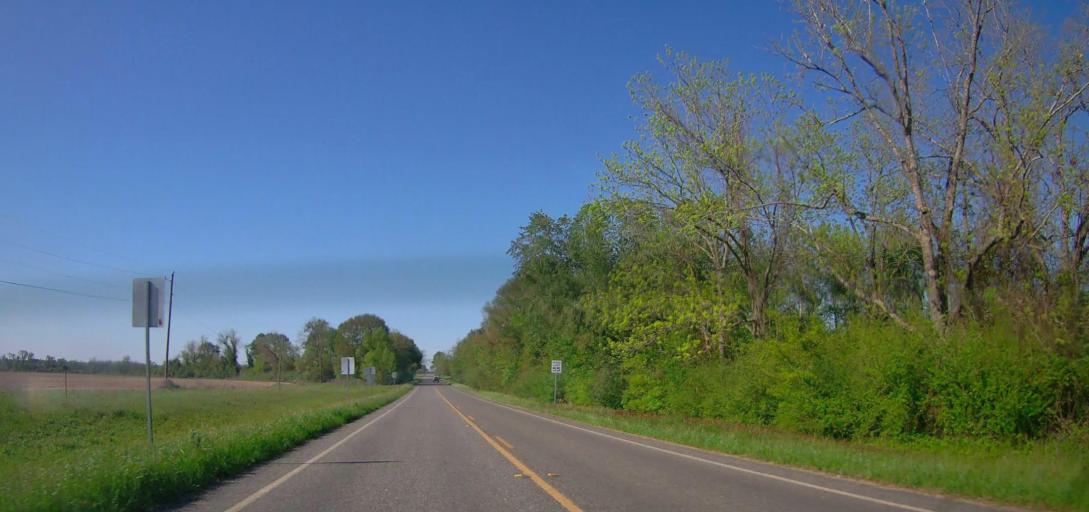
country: US
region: Georgia
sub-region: Wilcox County
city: Rochelle
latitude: 31.9609
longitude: -83.4563
